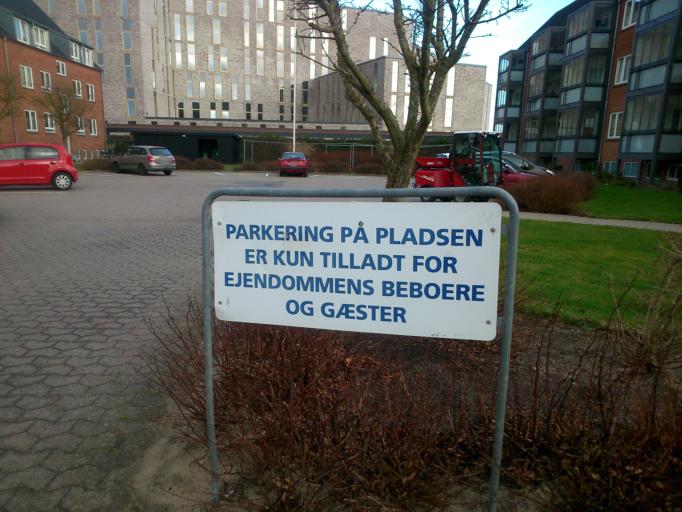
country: DK
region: Central Jutland
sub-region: Holstebro Kommune
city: Holstebro
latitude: 56.3698
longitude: 8.6245
